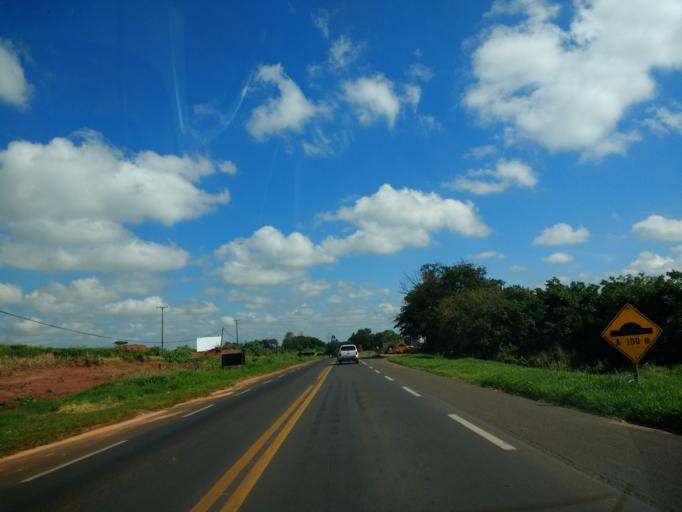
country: BR
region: Parana
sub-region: Umuarama
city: Umuarama
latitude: -23.8136
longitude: -53.3278
